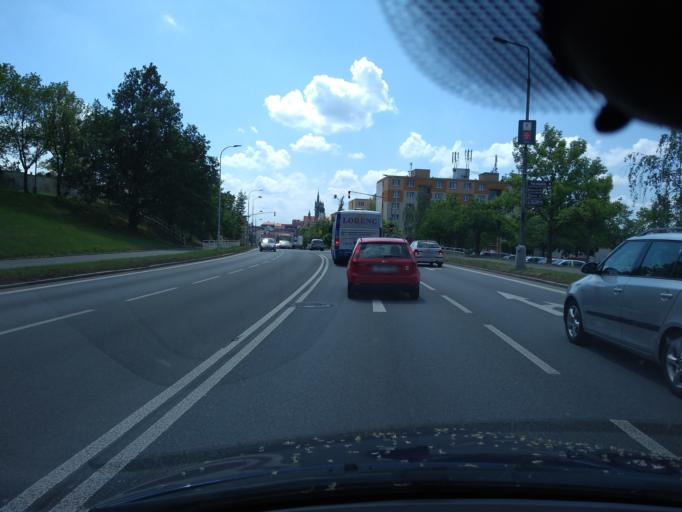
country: CZ
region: Plzensky
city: Klatovy
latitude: 49.4023
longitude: 13.2929
